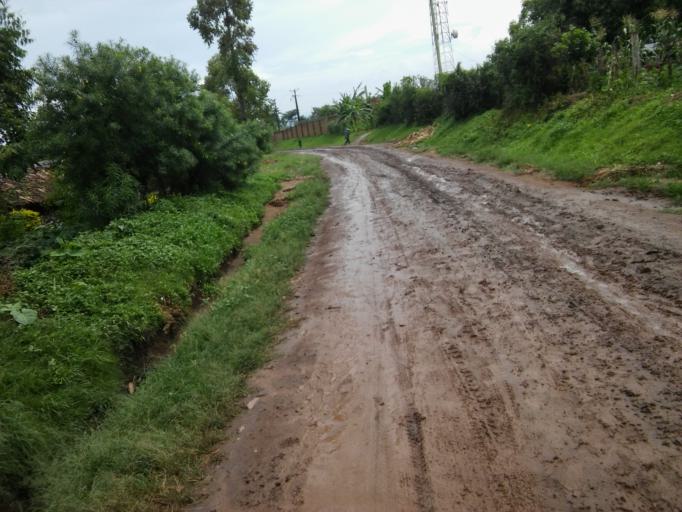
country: UG
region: Eastern Region
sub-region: Mbale District
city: Mbale
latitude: 1.0374
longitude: 34.2045
